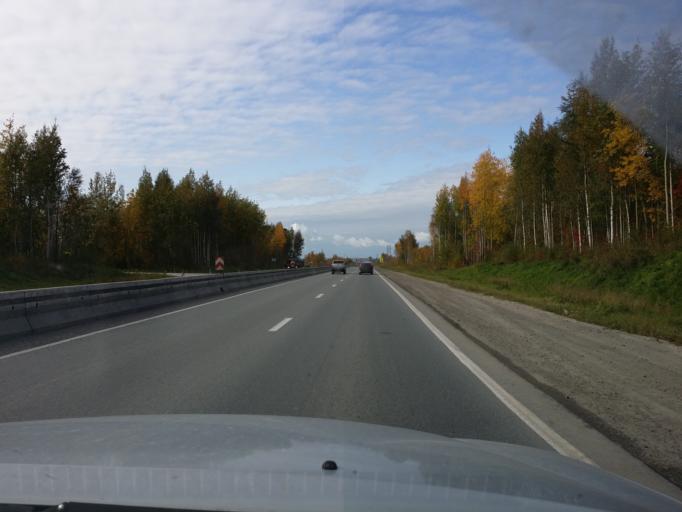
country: RU
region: Khanty-Mansiyskiy Avtonomnyy Okrug
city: Megion
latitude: 61.0570
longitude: 76.1546
